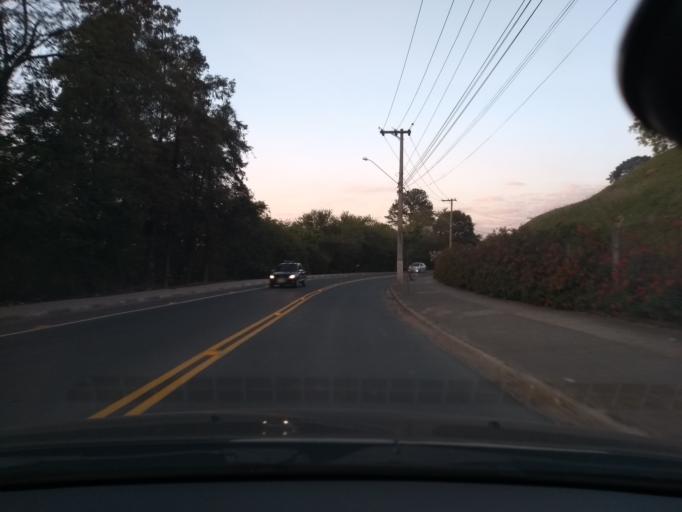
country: BR
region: Sao Paulo
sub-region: Itupeva
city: Itupeva
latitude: -23.1428
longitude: -47.0428
